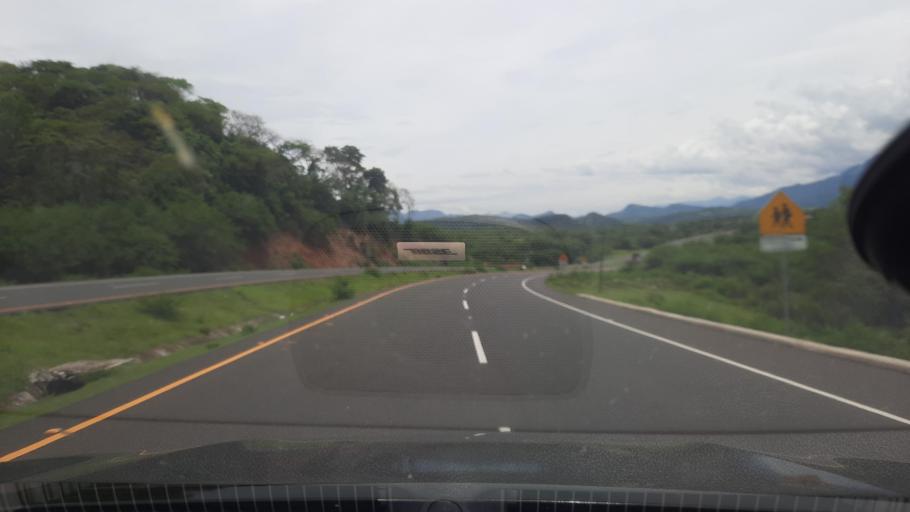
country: HN
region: Valle
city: Aramecina
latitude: 13.6966
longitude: -87.7156
